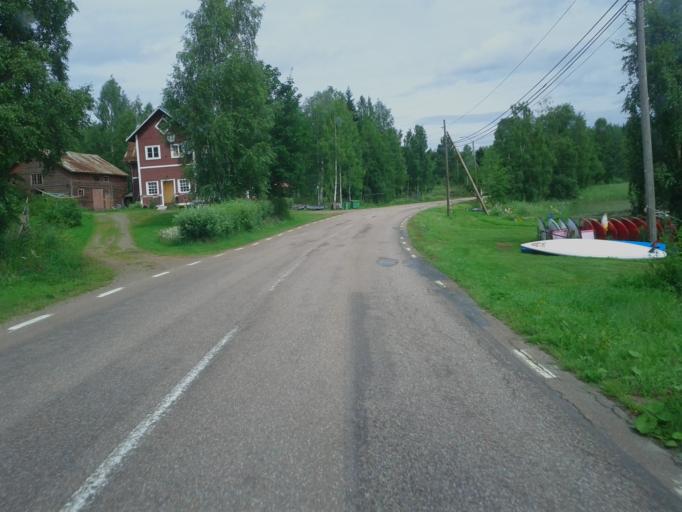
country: SE
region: Dalarna
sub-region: Smedjebackens Kommun
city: Smedjebacken
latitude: 60.3122
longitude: 15.3733
